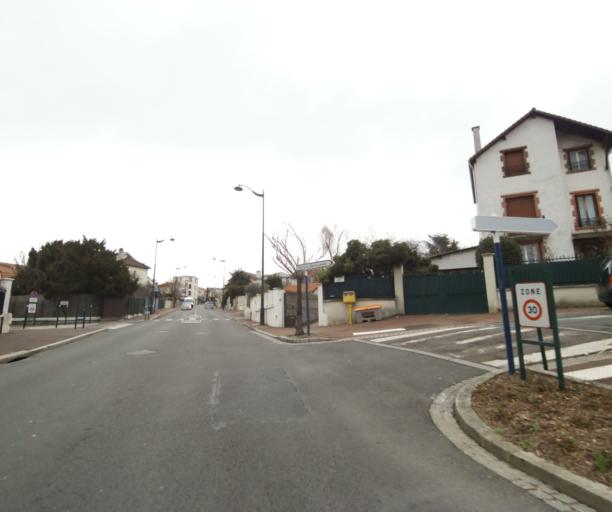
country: FR
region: Ile-de-France
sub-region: Departement des Hauts-de-Seine
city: Rueil-Malmaison
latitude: 48.8785
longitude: 2.1915
